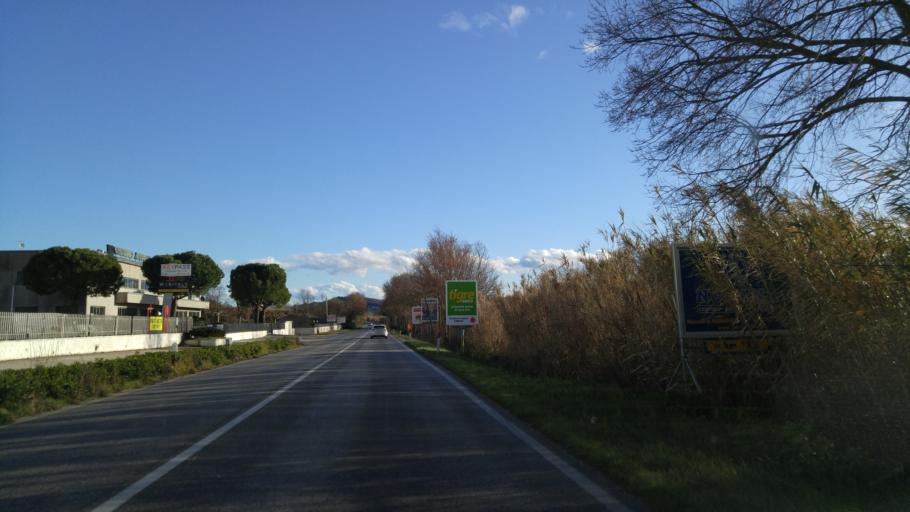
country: IT
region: The Marches
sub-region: Provincia di Ancona
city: Camerano
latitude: 43.5124
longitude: 13.5414
